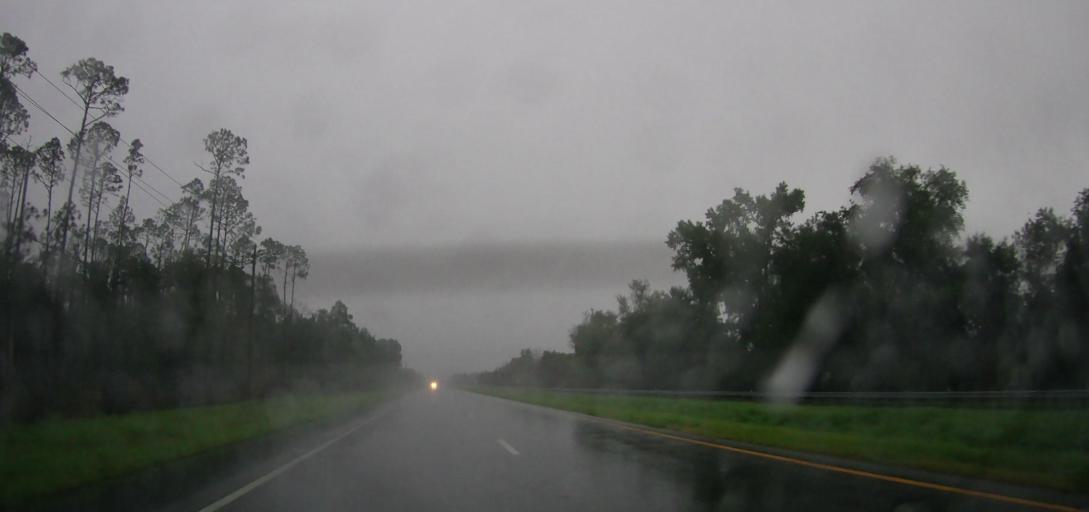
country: US
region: Georgia
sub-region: Clinch County
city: Homerville
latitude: 31.0493
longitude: -82.7132
